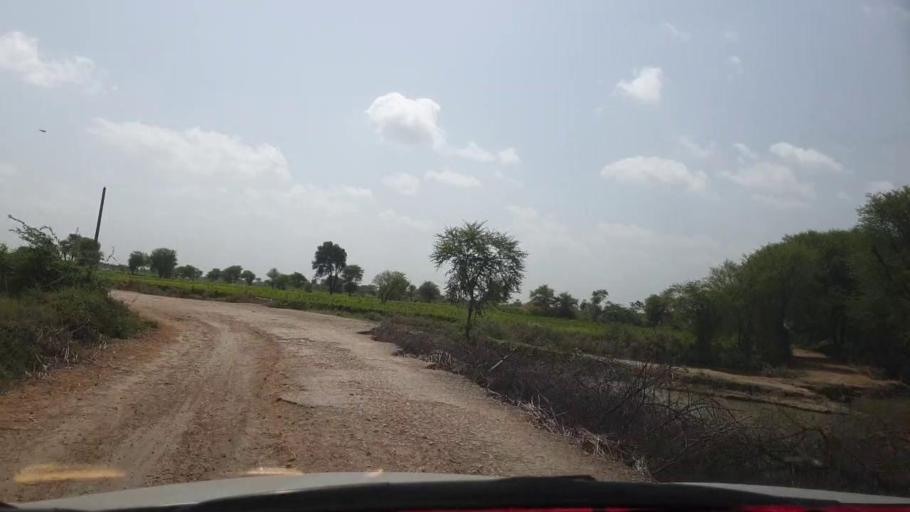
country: PK
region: Sindh
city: Talhar
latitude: 24.8959
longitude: 68.9060
